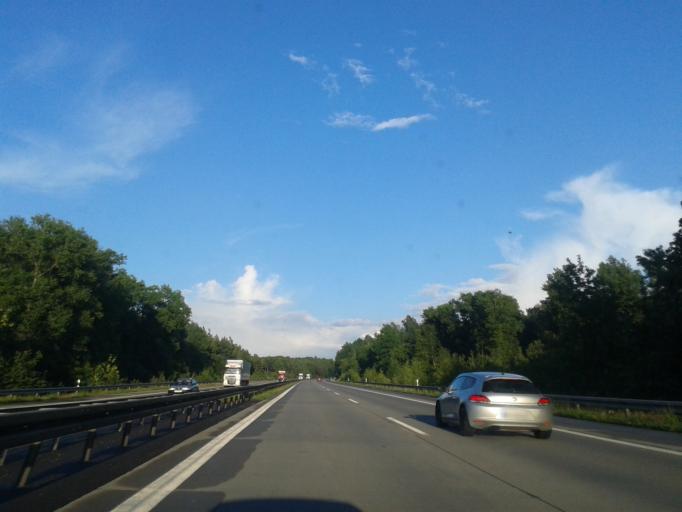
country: DE
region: Saxony
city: Naunhof
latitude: 51.2804
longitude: 12.6578
